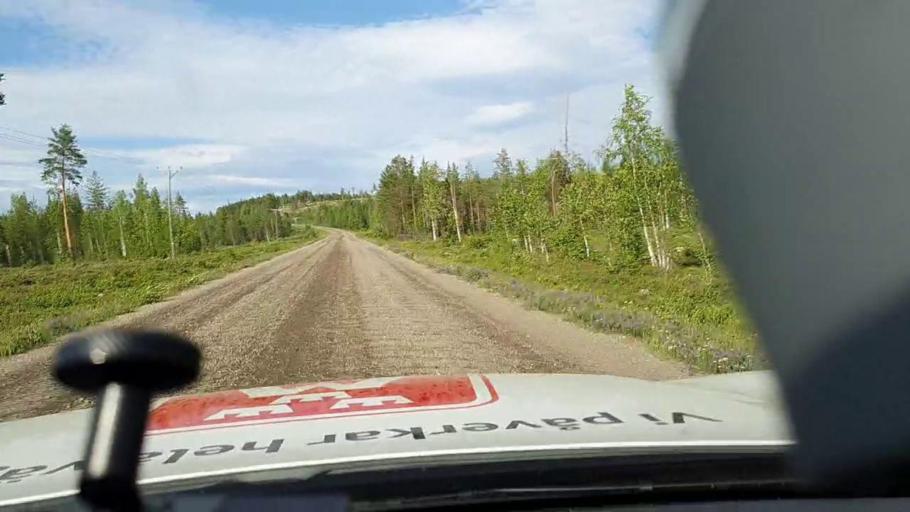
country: SE
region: Norrbotten
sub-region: Alvsbyns Kommun
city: AElvsbyn
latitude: 66.1626
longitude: 21.0511
